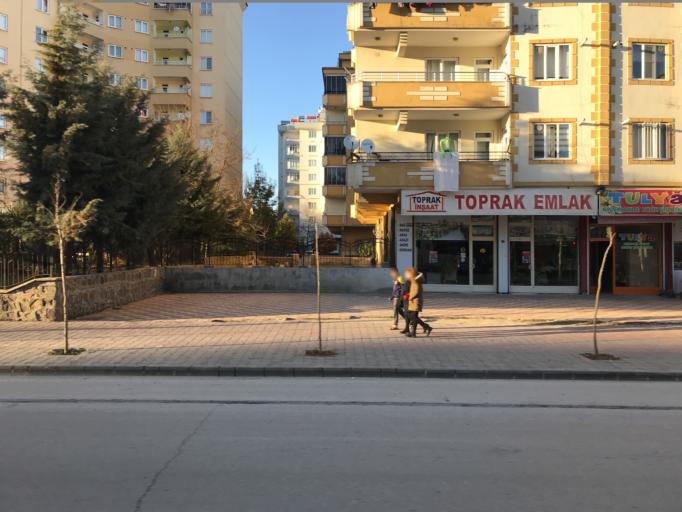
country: TR
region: Gaziantep
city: Sahinbey
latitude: 37.0153
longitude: 37.3554
